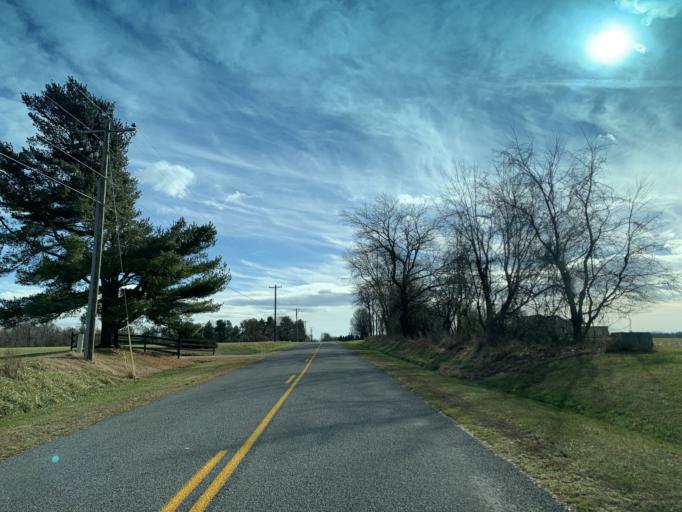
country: US
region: Maryland
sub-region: Kent County
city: Chestertown
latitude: 39.3416
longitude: -76.0509
